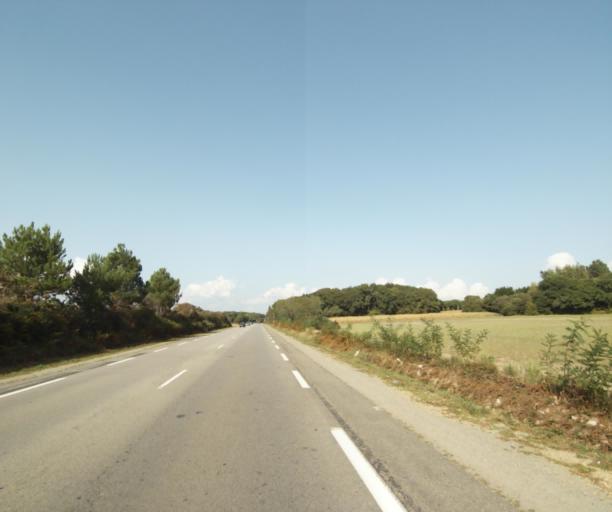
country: FR
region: Brittany
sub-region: Departement du Morbihan
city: Riantec
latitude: 47.7417
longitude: -3.3014
